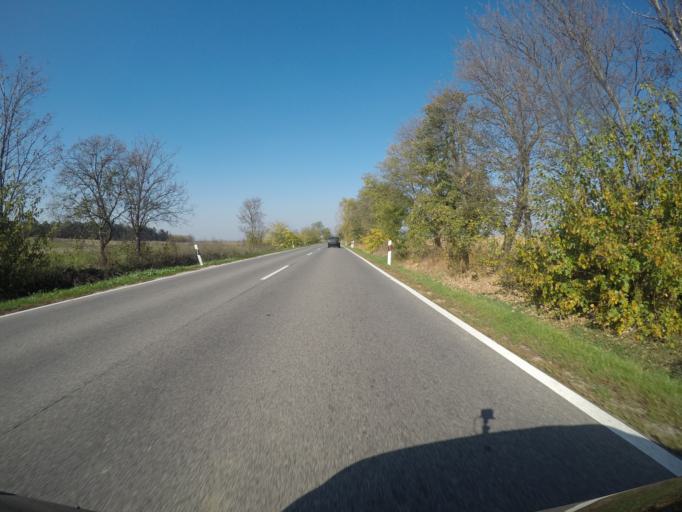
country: HU
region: Tolna
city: Tengelic
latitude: 46.5500
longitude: 18.6530
